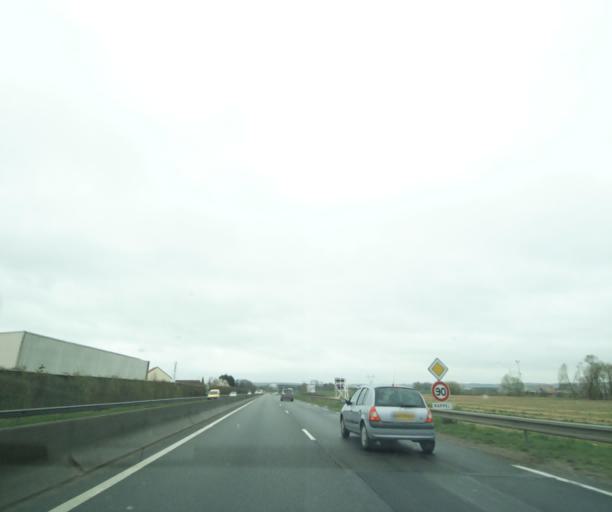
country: FR
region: Ile-de-France
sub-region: Departement de l'Essonne
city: Egly
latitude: 48.5794
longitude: 2.2347
